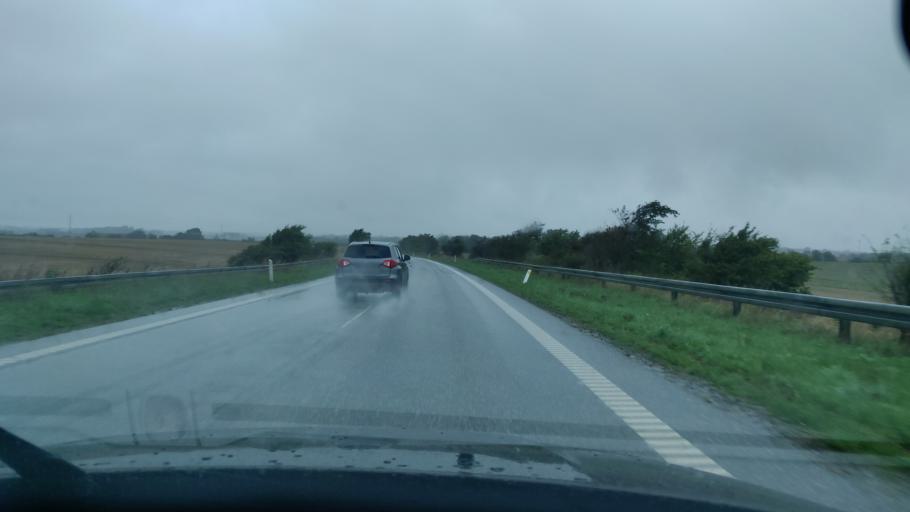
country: DK
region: North Denmark
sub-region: Thisted Kommune
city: Hurup
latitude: 56.8494
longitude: 8.5389
